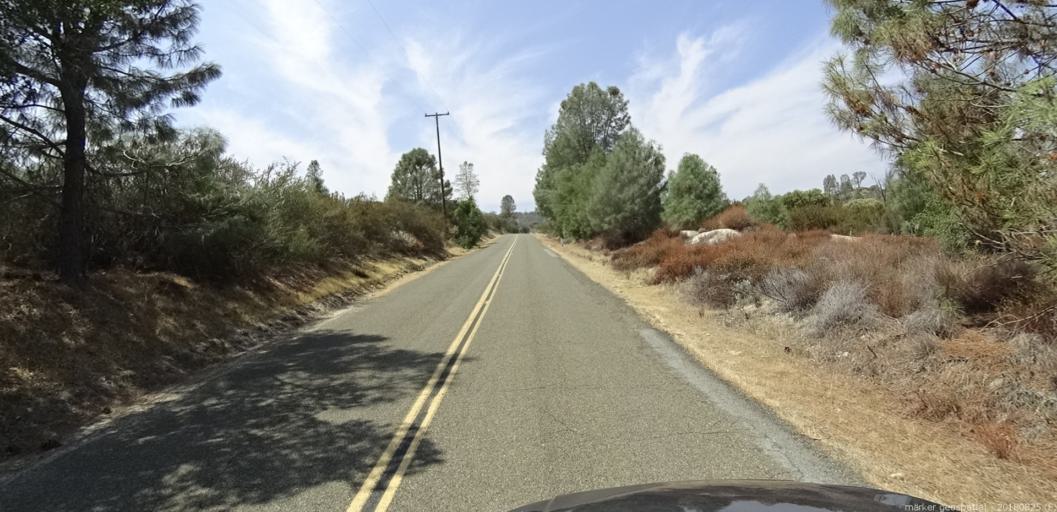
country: US
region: California
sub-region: San Luis Obispo County
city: San Miguel
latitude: 35.9207
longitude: -120.5190
